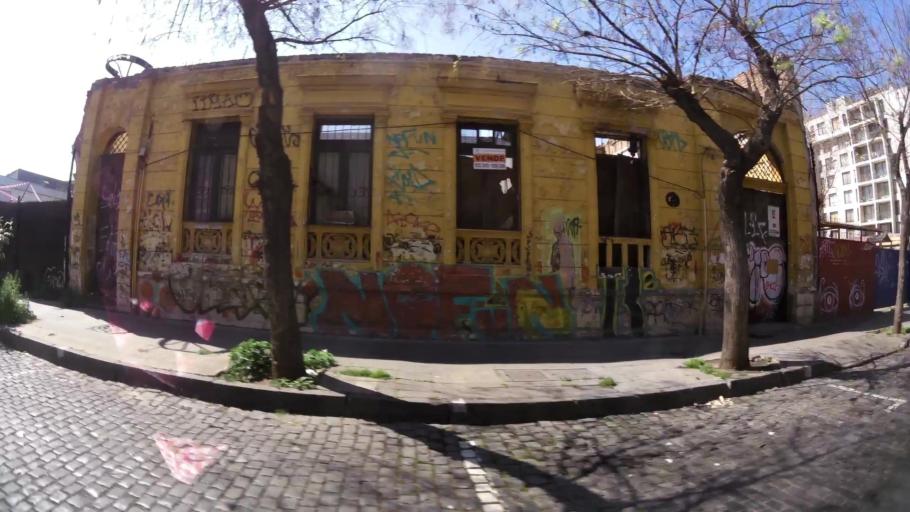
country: CL
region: Santiago Metropolitan
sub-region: Provincia de Santiago
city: Santiago
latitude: -33.4484
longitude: -70.6634
